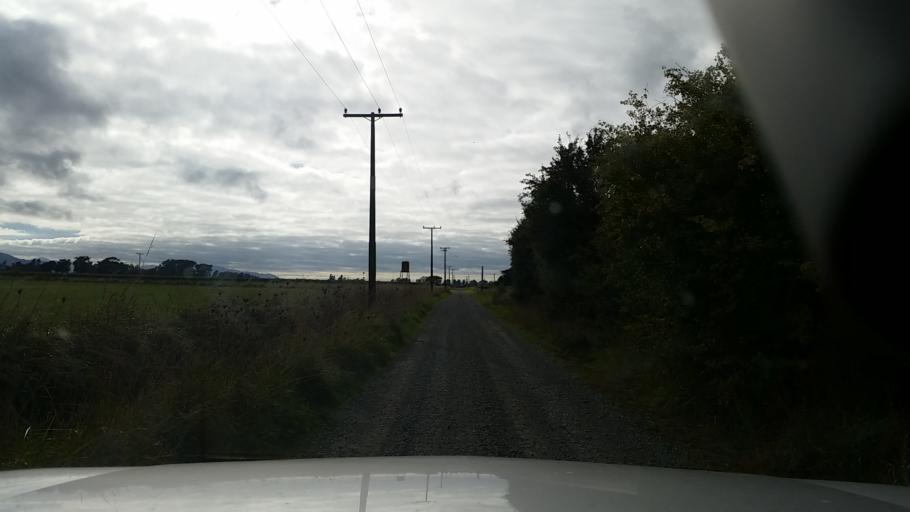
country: NZ
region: Marlborough
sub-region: Marlborough District
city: Blenheim
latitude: -41.4646
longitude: 173.9897
